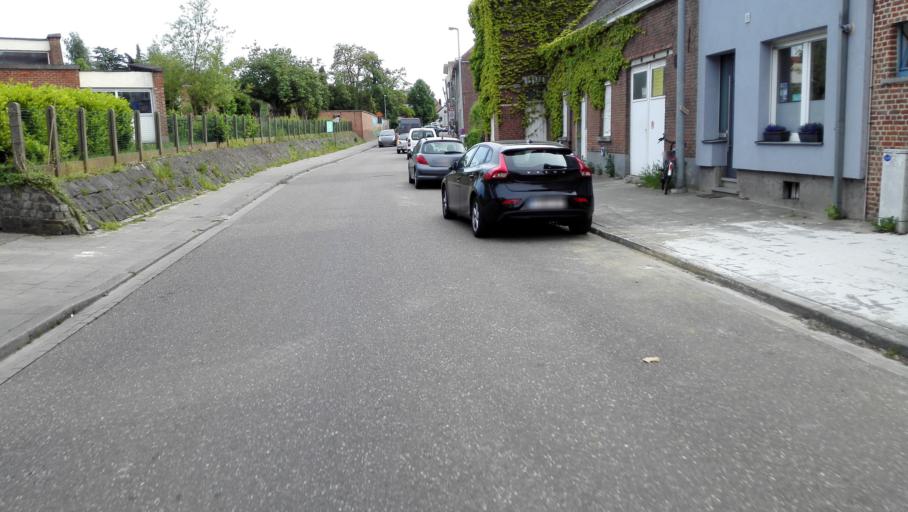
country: BE
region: Flanders
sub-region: Provincie Vlaams-Brabant
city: Leuven
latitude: 50.8924
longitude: 4.7302
